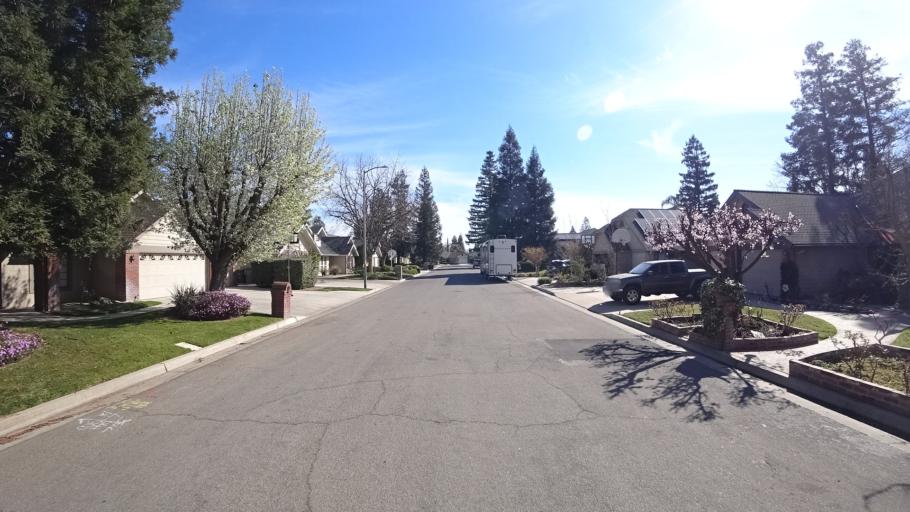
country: US
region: California
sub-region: Fresno County
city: Clovis
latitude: 36.8572
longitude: -119.7542
